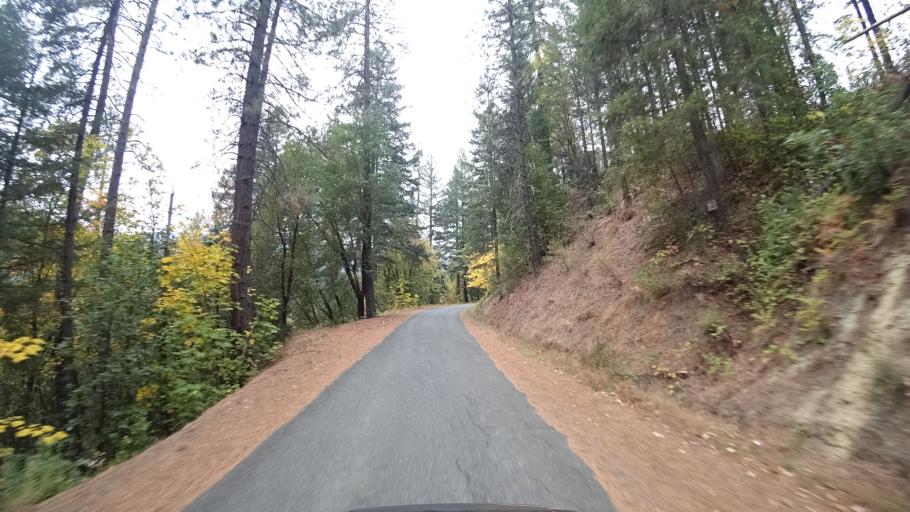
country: US
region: California
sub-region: Siskiyou County
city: Happy Camp
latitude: 41.7744
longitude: -123.3803
